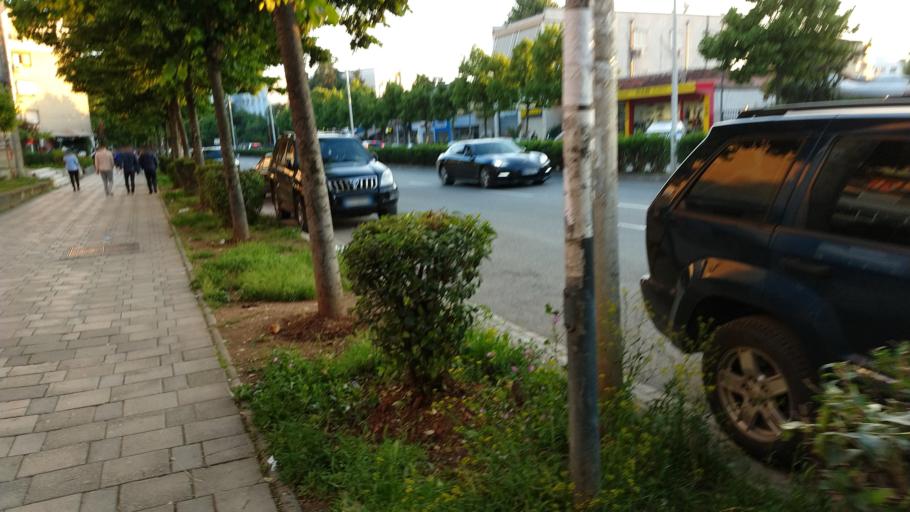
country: AL
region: Tirane
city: Tirana
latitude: 41.3302
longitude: 19.8034
